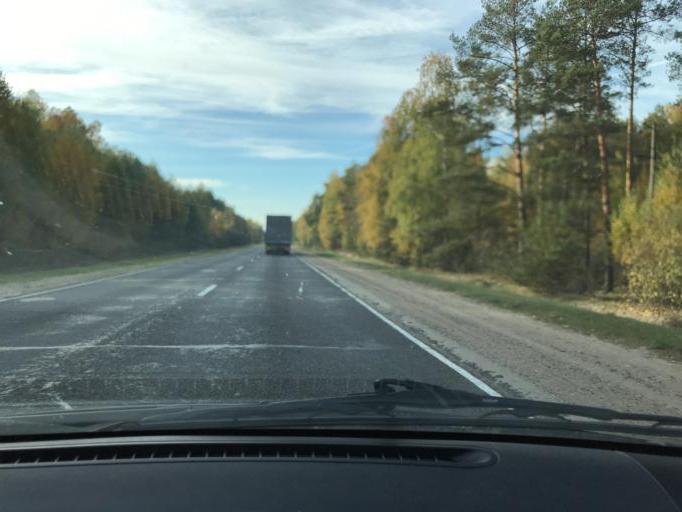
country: BY
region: Brest
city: Horad Pinsk
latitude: 52.1512
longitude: 25.8463
